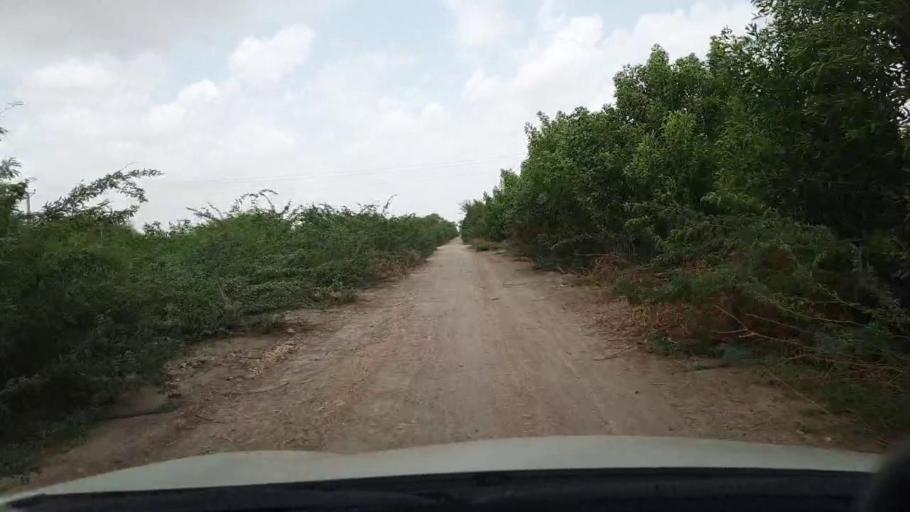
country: PK
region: Sindh
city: Kadhan
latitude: 24.3603
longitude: 68.9586
